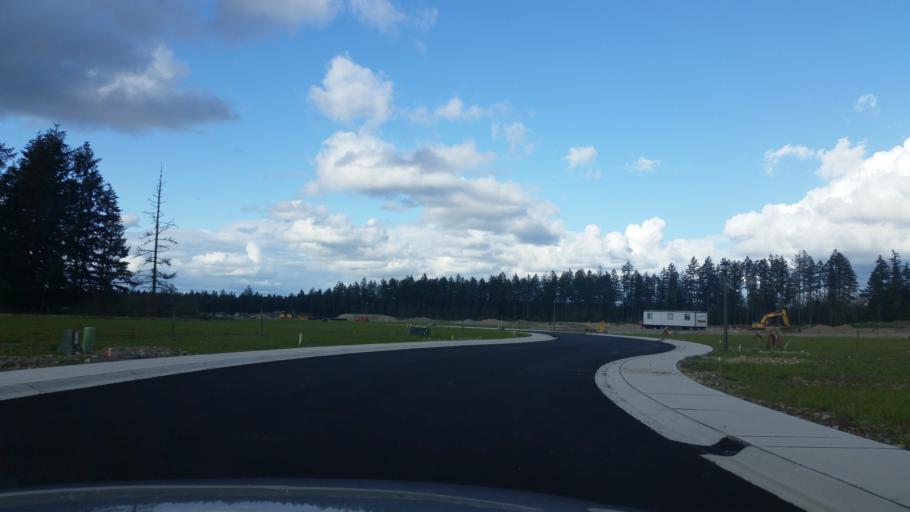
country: US
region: Washington
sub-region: Pierce County
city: Graham
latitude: 47.0825
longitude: -122.2773
